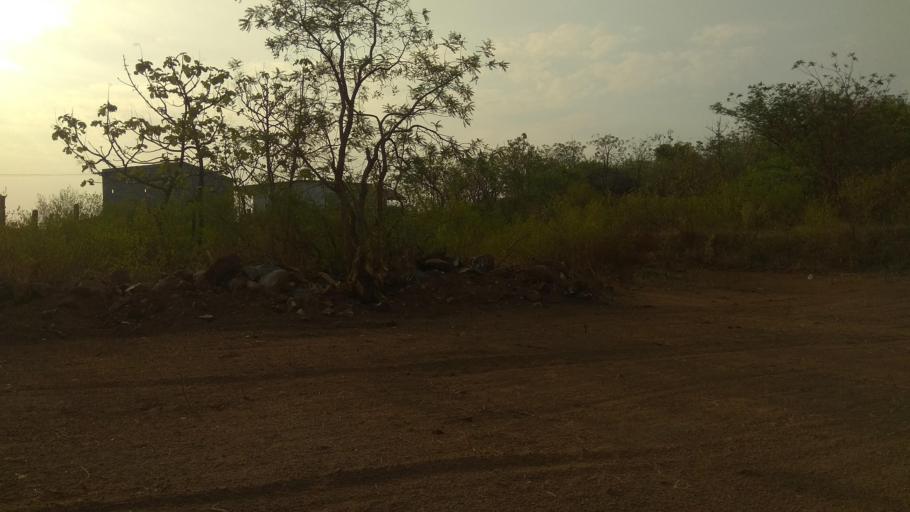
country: IN
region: Telangana
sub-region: Mahbubnagar
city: Farrukhnagar
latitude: 16.8943
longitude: 78.5042
